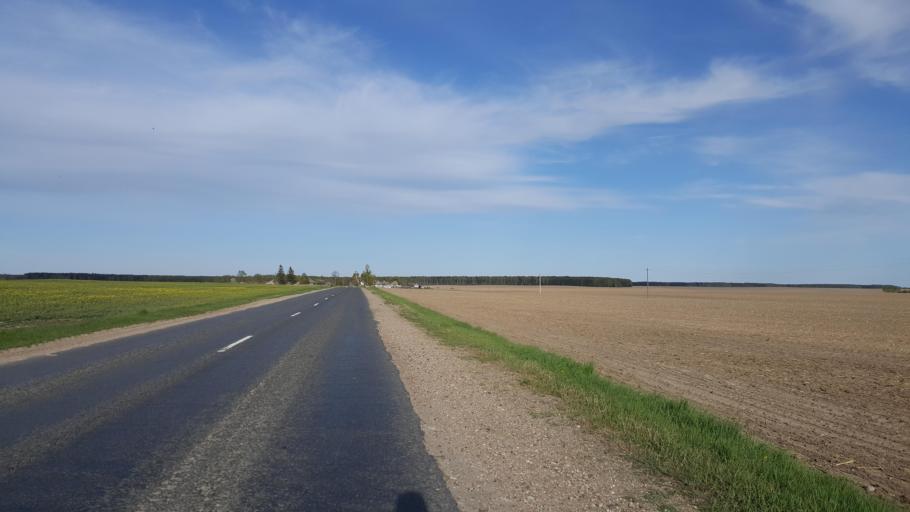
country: BY
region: Brest
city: Vysokaye
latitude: 52.4029
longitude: 23.5397
